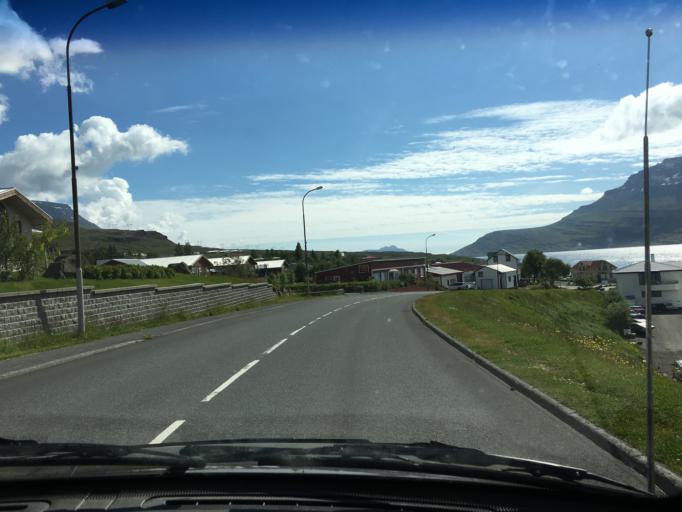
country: IS
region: East
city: Reydarfjoerdur
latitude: 65.0327
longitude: -14.2104
